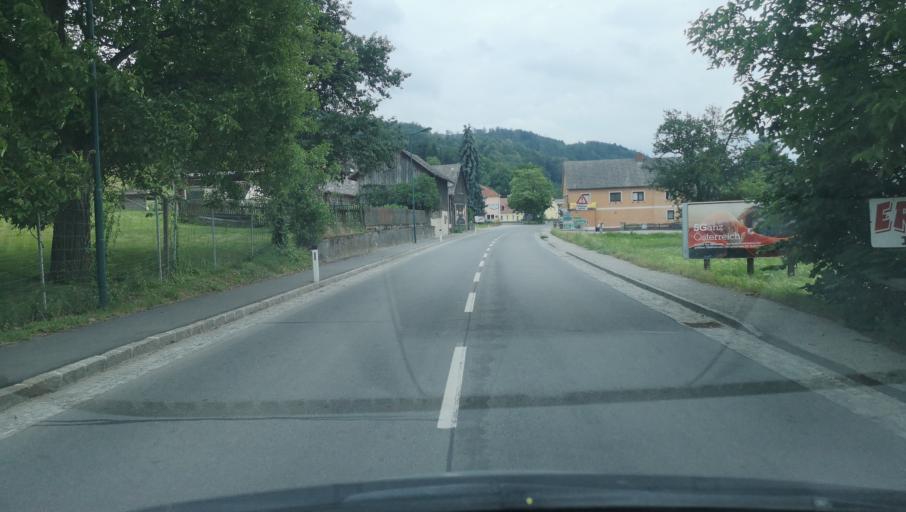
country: AT
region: Lower Austria
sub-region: Politischer Bezirk Melk
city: Ybbs an der Donau
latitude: 48.1955
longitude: 15.1052
